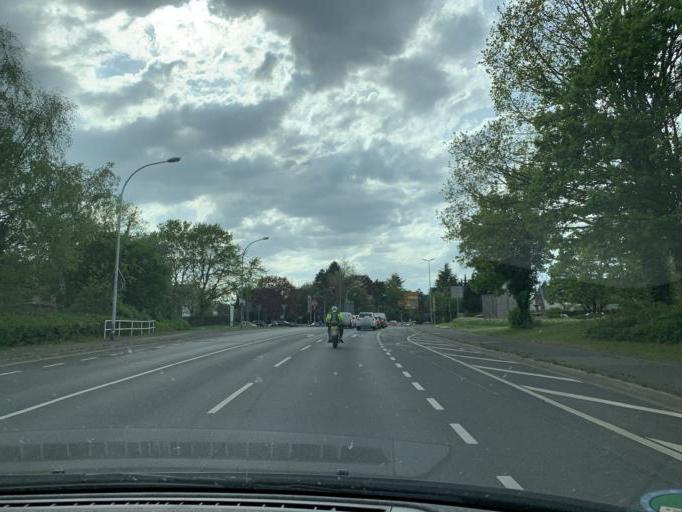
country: DE
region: North Rhine-Westphalia
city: Bruhl
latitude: 50.8311
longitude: 6.8963
